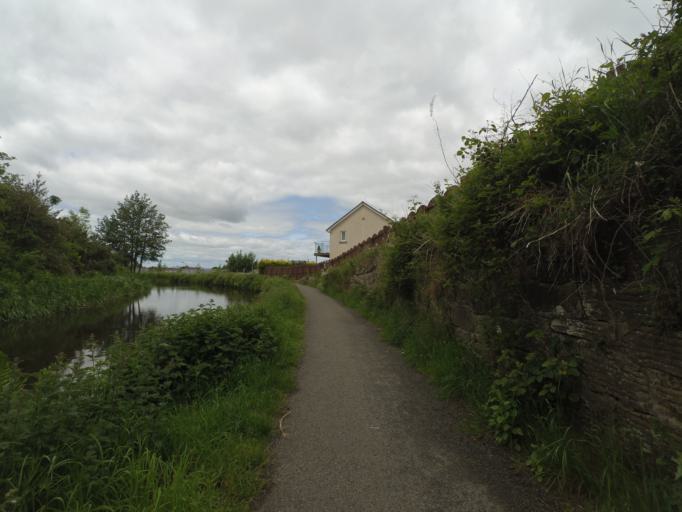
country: GB
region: Scotland
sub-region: Falkirk
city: Polmont
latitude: 55.9841
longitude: -3.7182
